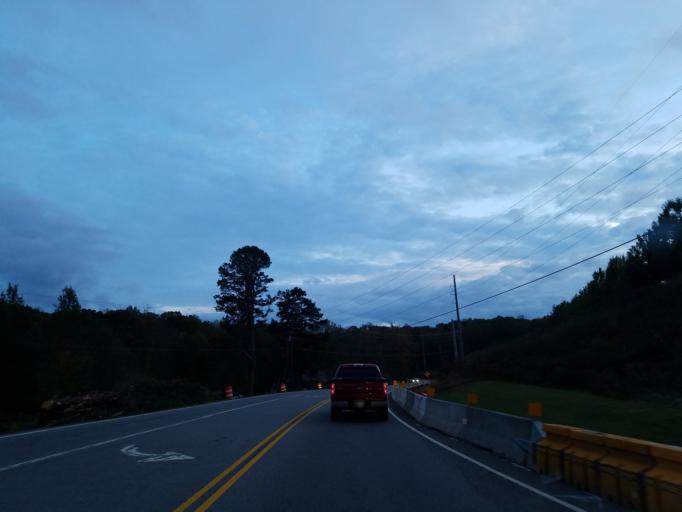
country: US
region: Georgia
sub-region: Dawson County
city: Dawsonville
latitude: 34.3552
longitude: -84.1136
